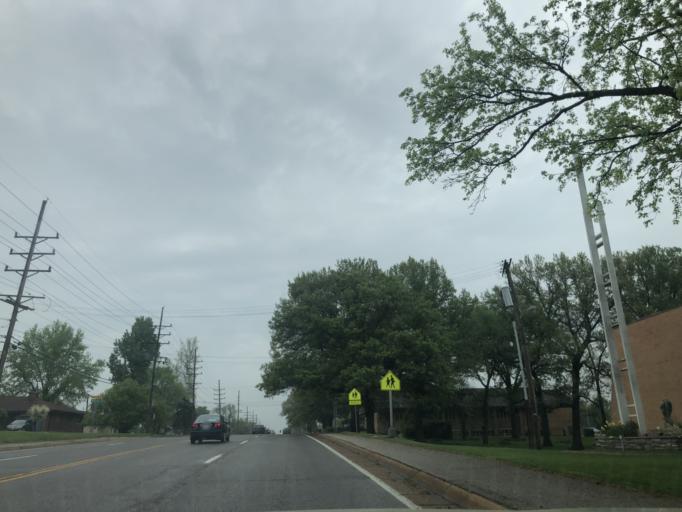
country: US
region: Missouri
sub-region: Saint Louis County
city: Marlborough
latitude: 38.5669
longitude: -90.3205
